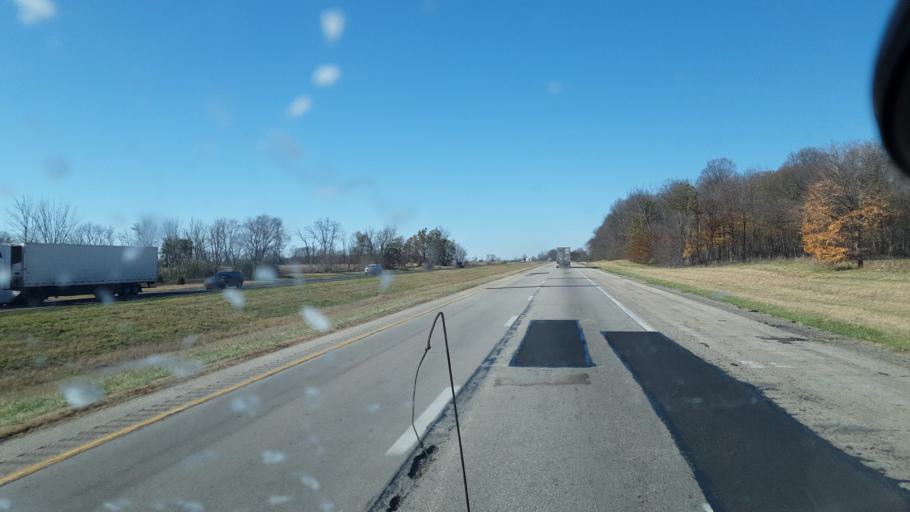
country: US
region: Ohio
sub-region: Preble County
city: New Paris
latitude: 39.8359
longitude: -84.6985
